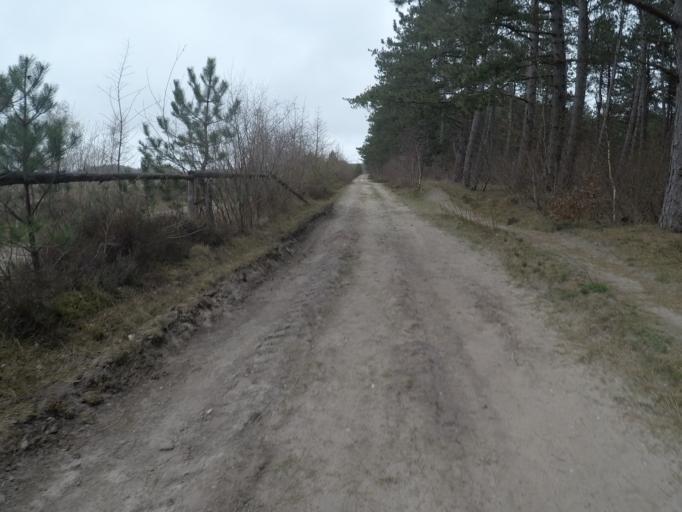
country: DE
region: Lower Saxony
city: Nordholz
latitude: 53.8242
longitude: 8.6443
